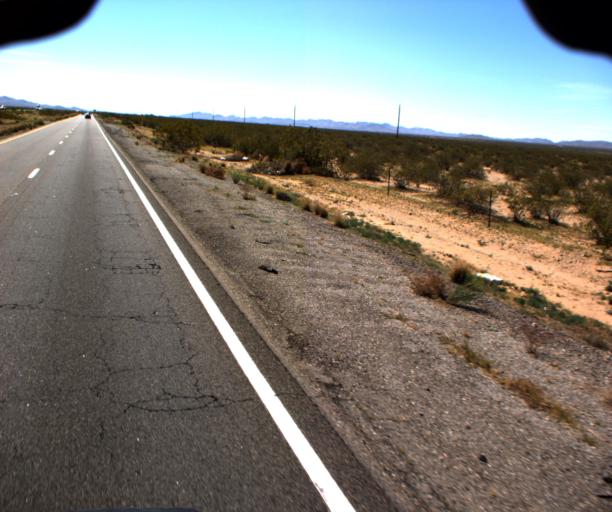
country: US
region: Arizona
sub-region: Mohave County
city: Dolan Springs
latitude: 35.5839
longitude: -114.3903
